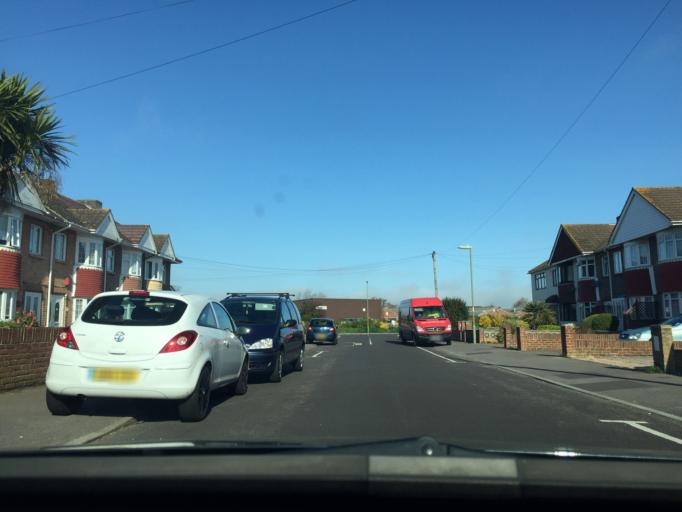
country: GB
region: England
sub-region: Hampshire
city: Gosport
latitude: 50.8152
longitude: -1.1499
